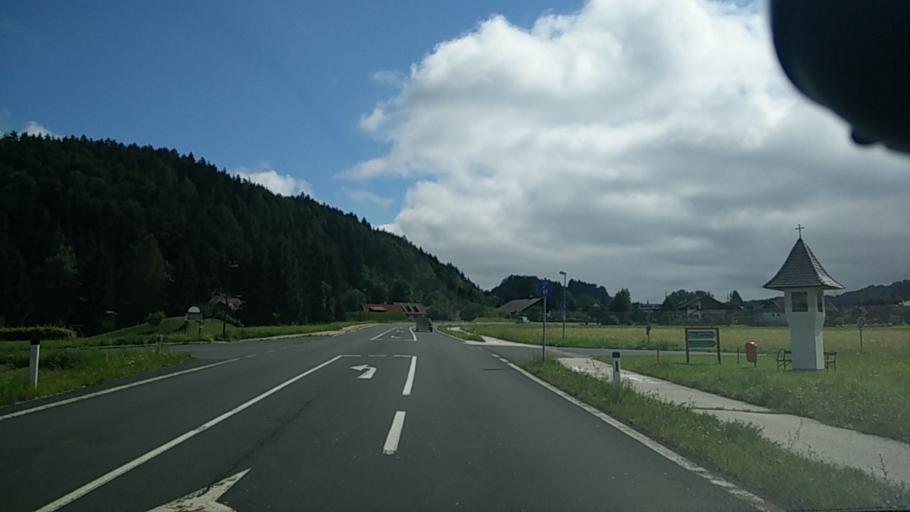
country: AT
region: Carinthia
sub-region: Politischer Bezirk Villach Land
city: Finkenstein am Faaker See
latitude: 46.5594
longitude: 13.9138
